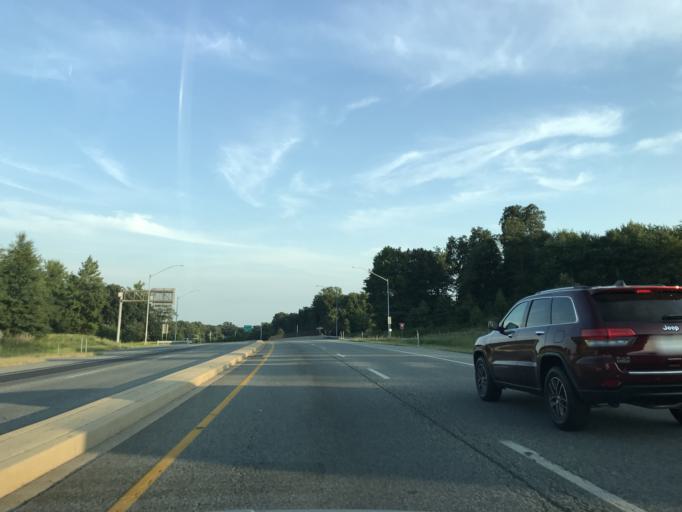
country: US
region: Maryland
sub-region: Cecil County
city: North East
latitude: 39.6338
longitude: -75.9576
